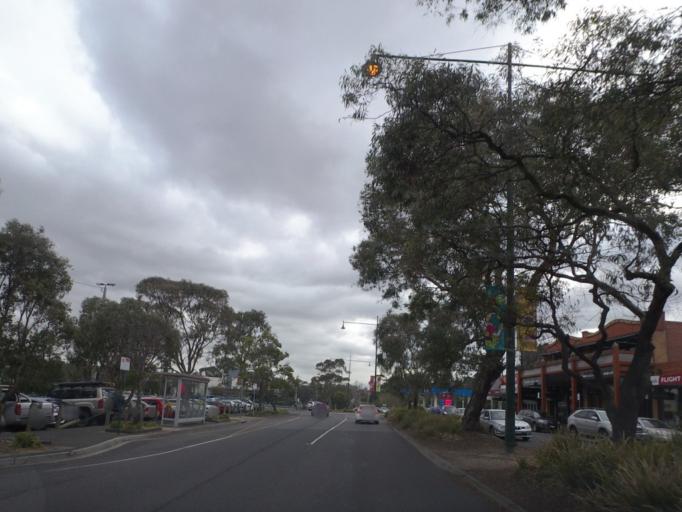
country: AU
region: Victoria
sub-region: Nillumbik
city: Eltham North
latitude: -37.7130
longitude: 145.1487
